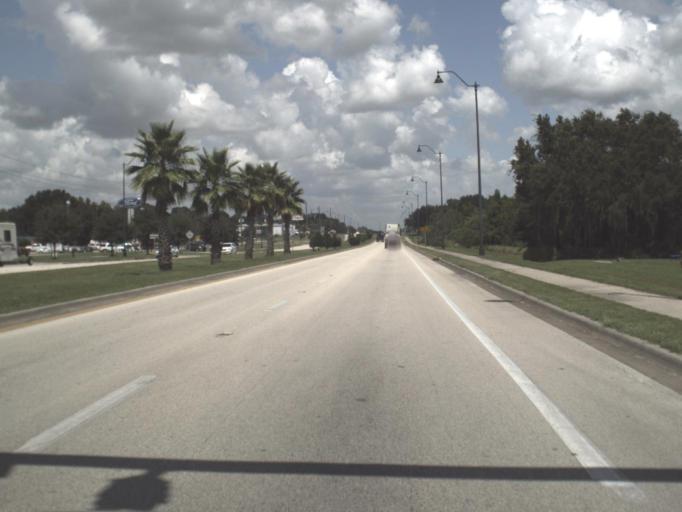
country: US
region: Florida
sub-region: Hardee County
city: Wauchula
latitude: 27.5575
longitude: -81.8129
